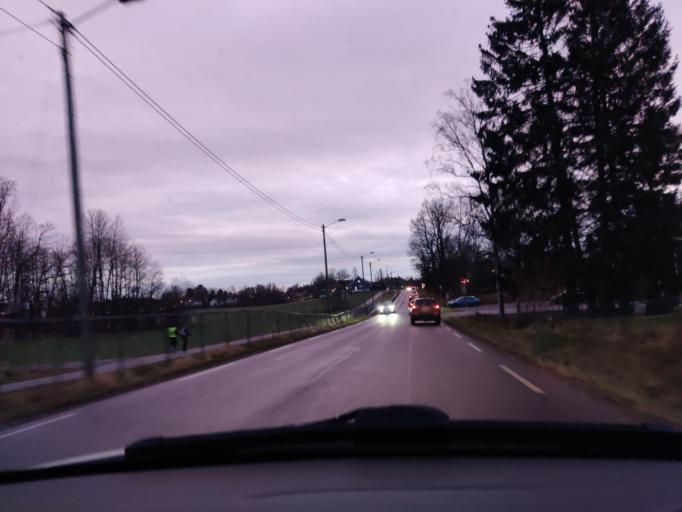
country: NO
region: Vestfold
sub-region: Tonsberg
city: Sem
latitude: 59.2598
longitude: 10.3614
